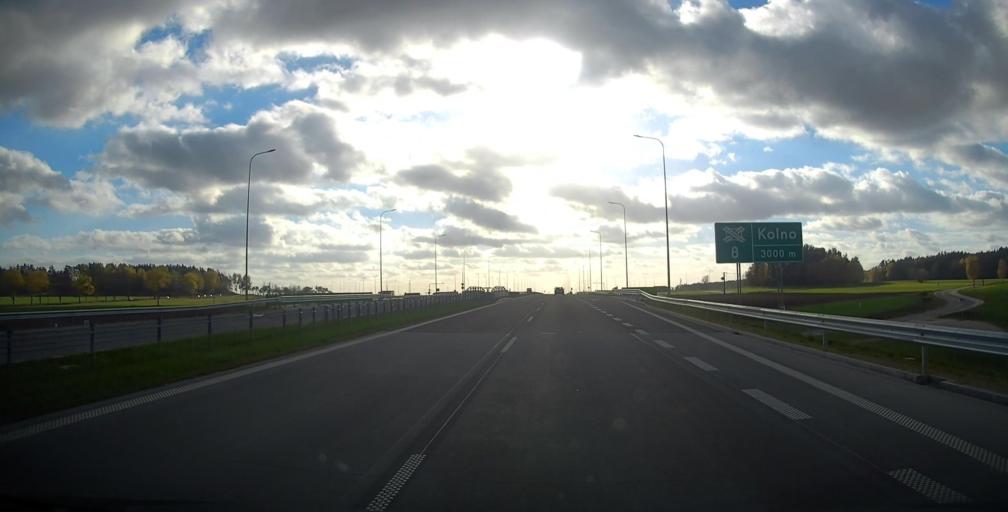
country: PL
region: Podlasie
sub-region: Powiat lomzynski
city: Piatnica
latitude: 53.2739
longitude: 22.1296
